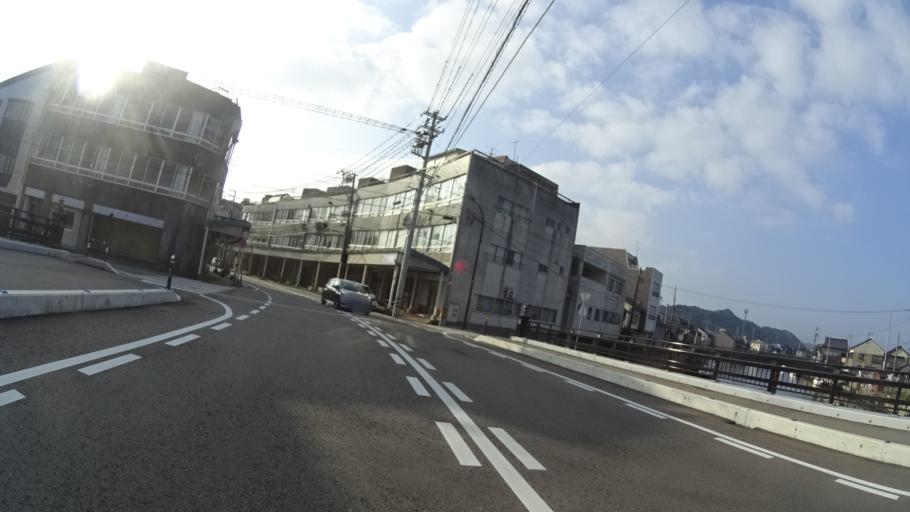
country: JP
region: Toyama
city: Himi
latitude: 36.8613
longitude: 136.9856
